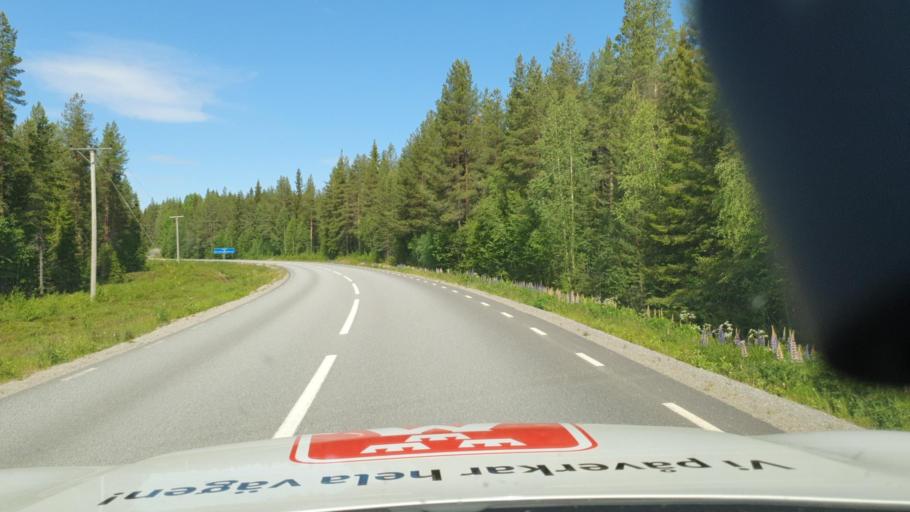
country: SE
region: Vaesterbotten
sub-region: Skelleftea Kommun
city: Langsele
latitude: 64.7492
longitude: 20.3489
